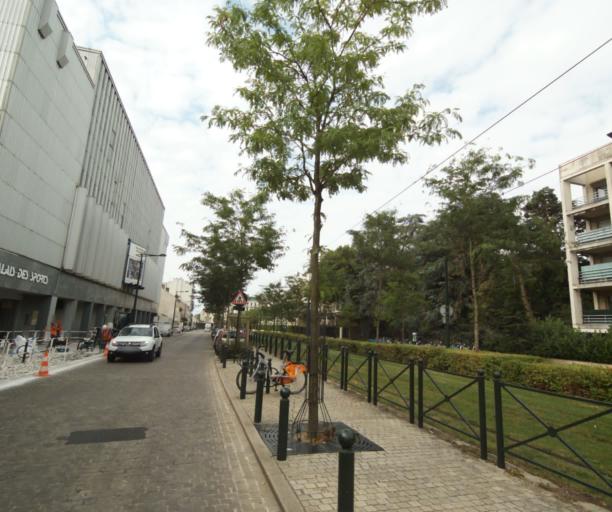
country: FR
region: Centre
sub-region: Departement du Loiret
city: Orleans
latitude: 47.9105
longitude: 1.9118
